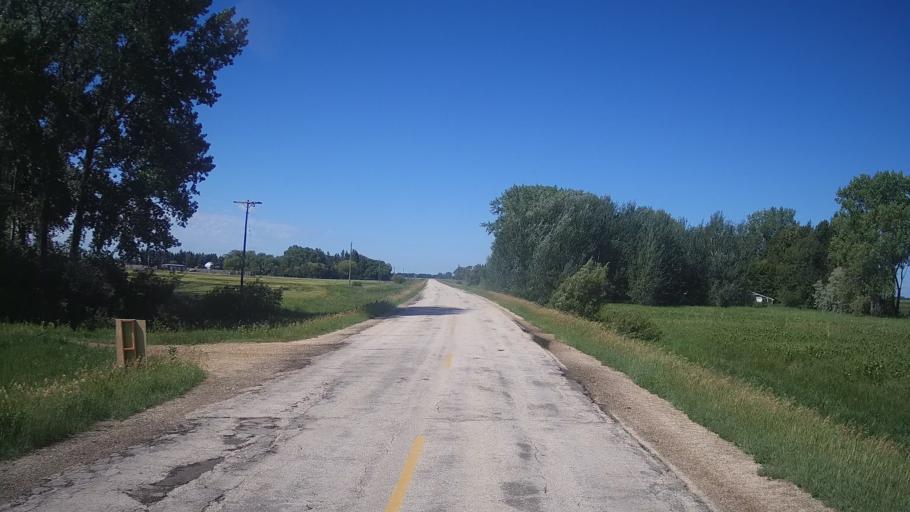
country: CA
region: Manitoba
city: Portage la Prairie
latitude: 50.0400
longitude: -98.0706
